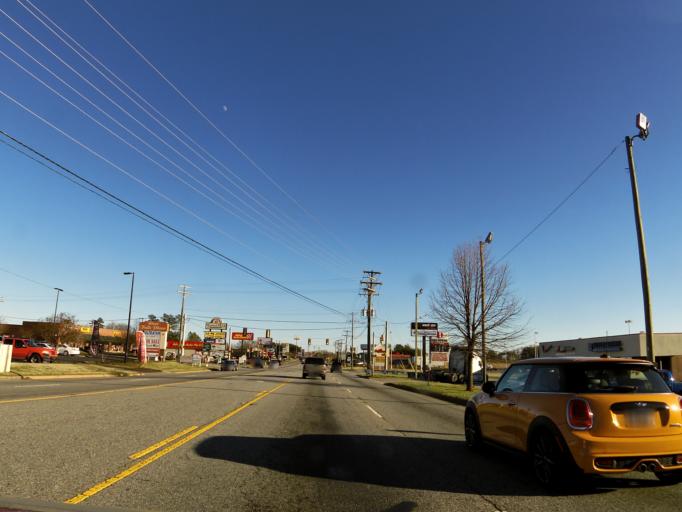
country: US
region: South Carolina
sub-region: Spartanburg County
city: Wellford
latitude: 34.8891
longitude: -82.0722
